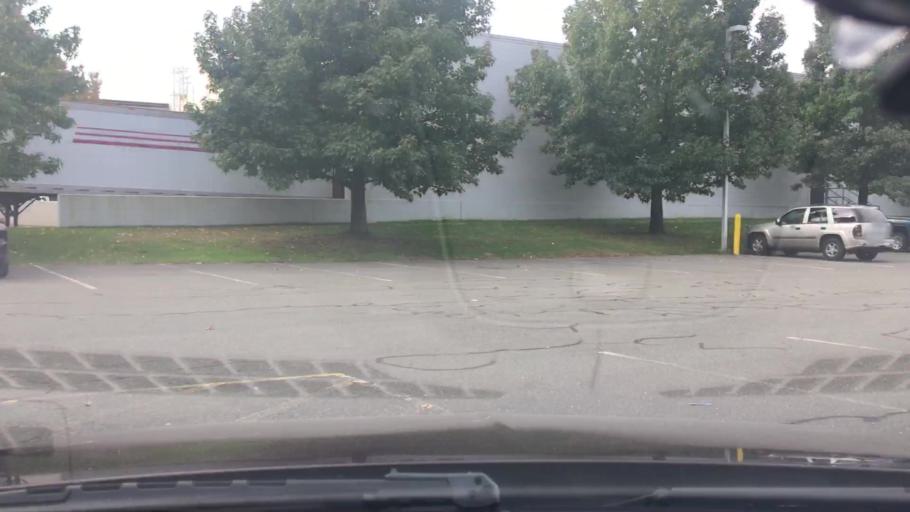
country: US
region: Connecticut
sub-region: Hartford County
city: South Windsor
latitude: 41.8318
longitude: -72.6071
